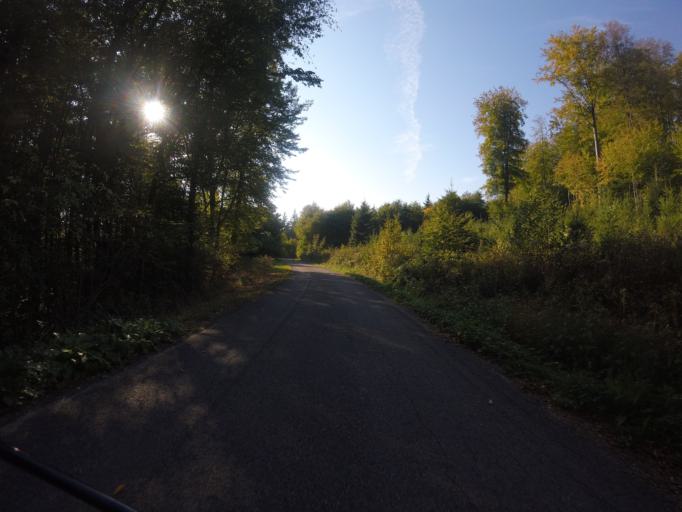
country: DE
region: Baden-Wuerttemberg
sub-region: Regierungsbezirk Stuttgart
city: Oppenweiler
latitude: 48.9850
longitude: 9.4270
